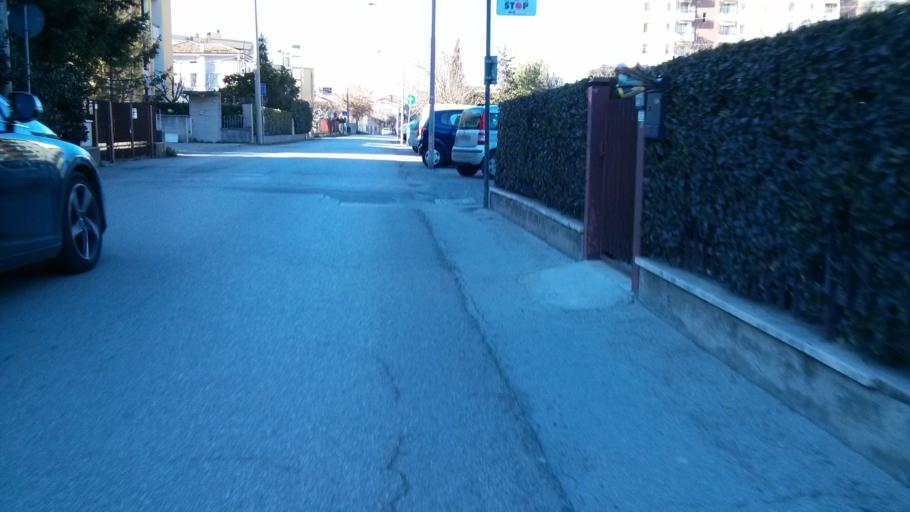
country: IT
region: The Marches
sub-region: Provincia di Pesaro e Urbino
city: Fano
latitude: 43.8343
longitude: 13.0262
